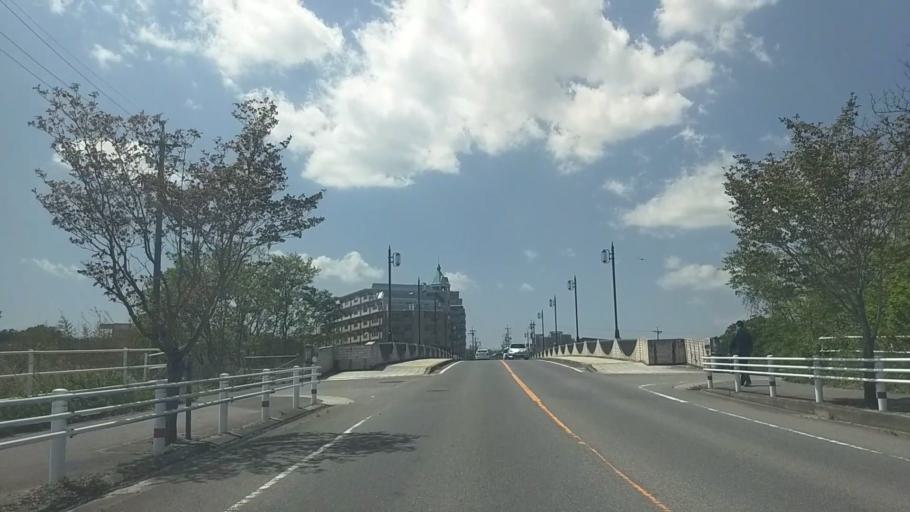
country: JP
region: Aichi
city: Okazaki
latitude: 34.9399
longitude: 137.1872
